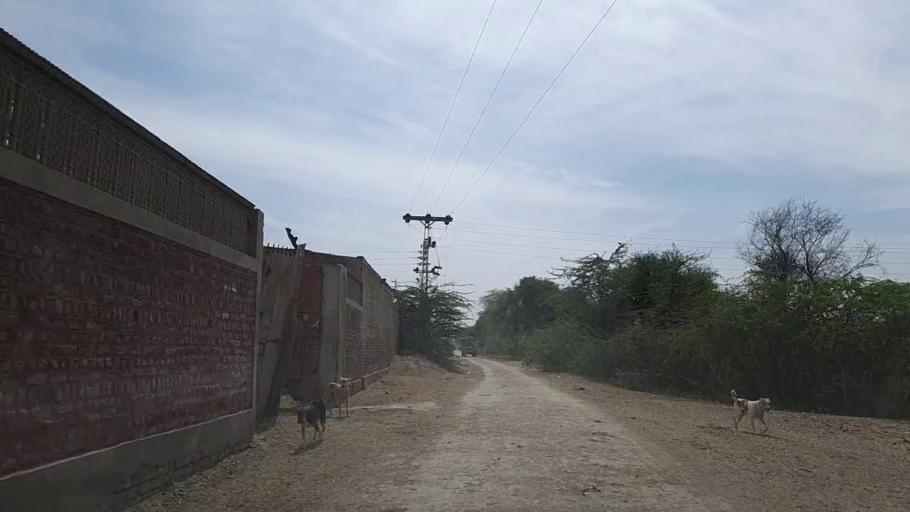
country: PK
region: Sindh
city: Samaro
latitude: 25.2647
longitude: 69.4535
